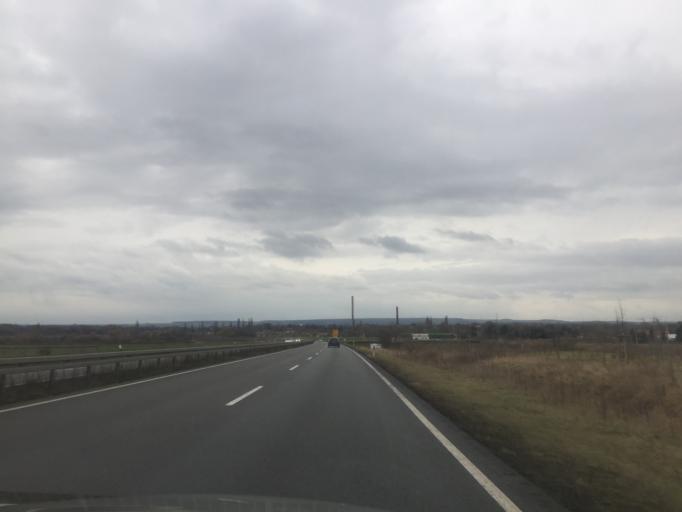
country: DE
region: Saxony-Anhalt
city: Egeln
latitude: 51.9659
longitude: 11.4525
